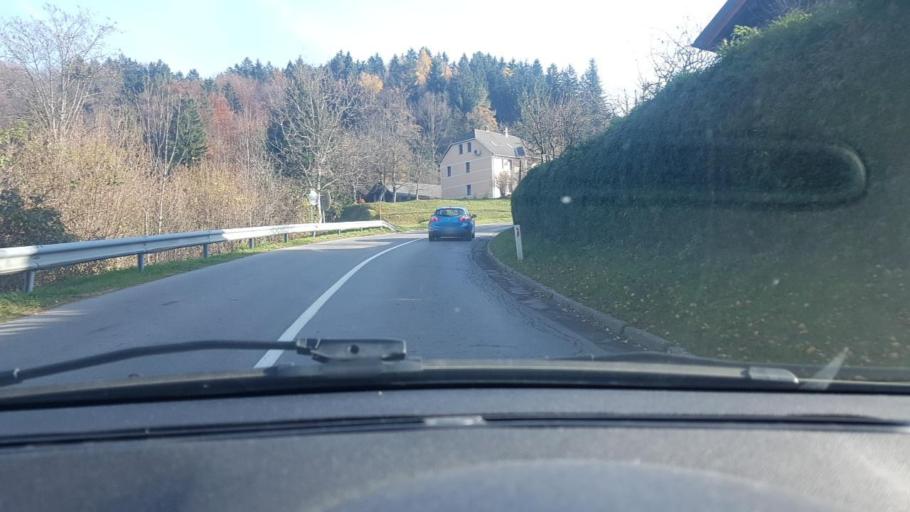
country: SI
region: Trzic
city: Bistrica pri Trzicu
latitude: 46.3373
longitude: 14.3053
